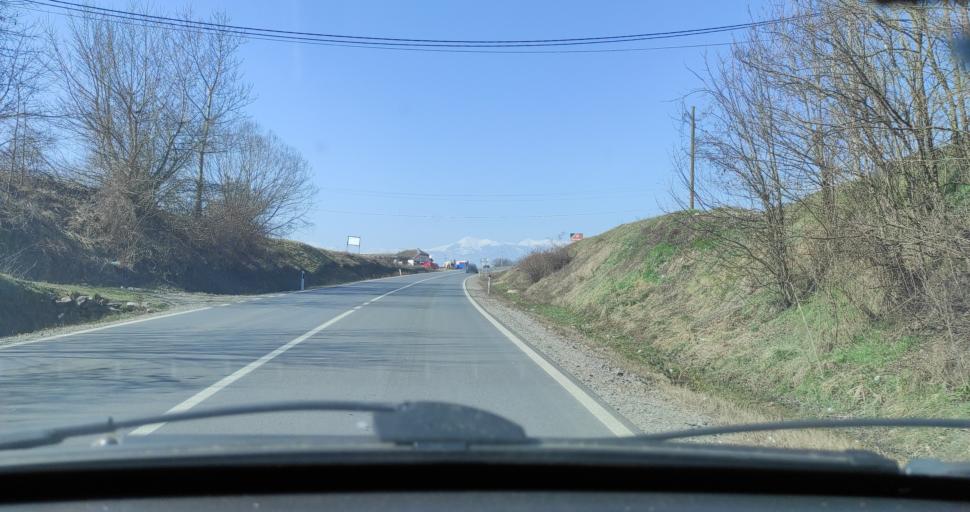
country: XK
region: Pec
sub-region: Komuna e Klines
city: Klina
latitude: 42.5902
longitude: 20.5586
